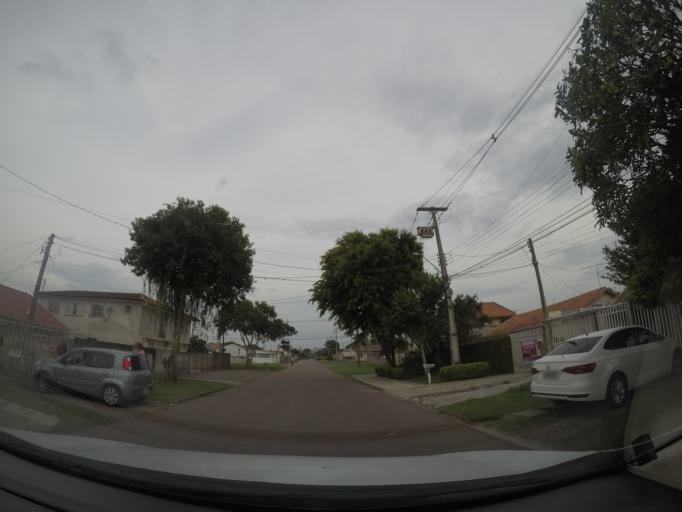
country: BR
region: Parana
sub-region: Sao Jose Dos Pinhais
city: Sao Jose dos Pinhais
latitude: -25.5168
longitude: -49.2232
